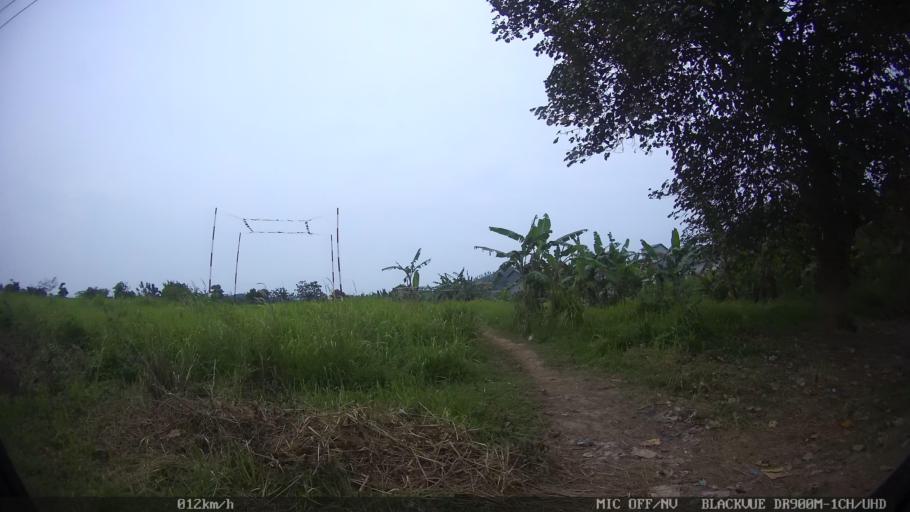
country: ID
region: Lampung
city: Panjang
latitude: -5.4342
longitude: 105.3316
